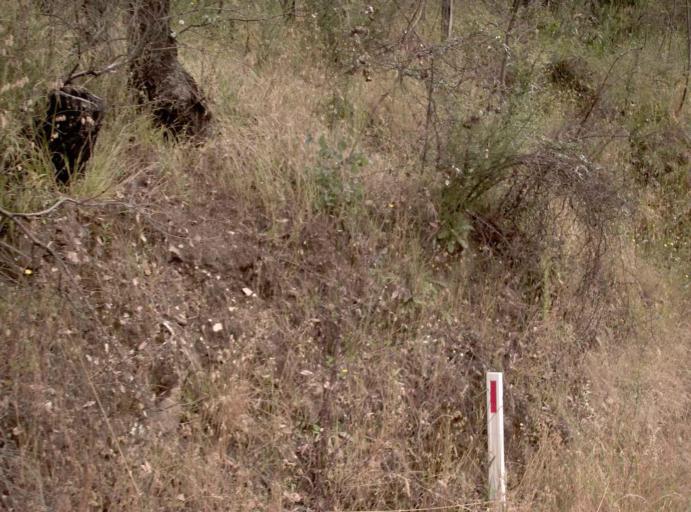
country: AU
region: Victoria
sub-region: Wellington
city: Heyfield
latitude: -37.7439
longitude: 146.6661
